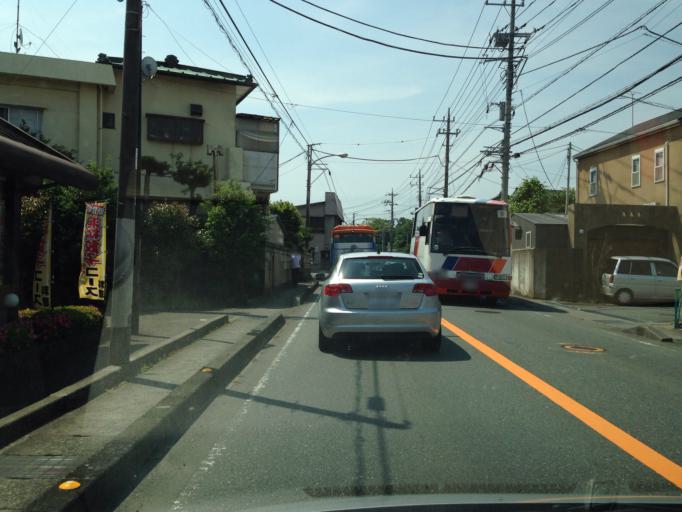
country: JP
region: Shizuoka
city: Numazu
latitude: 35.0744
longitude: 138.8731
